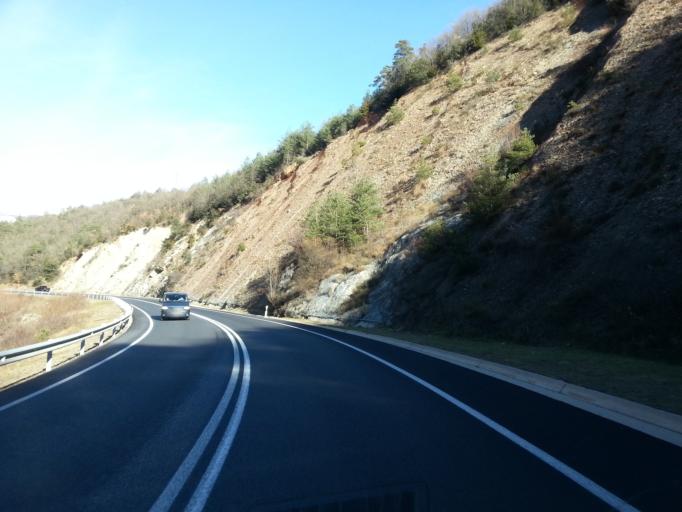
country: ES
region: Catalonia
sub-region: Provincia de Barcelona
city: Guardiola de Bergueda
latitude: 42.2079
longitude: 1.8688
